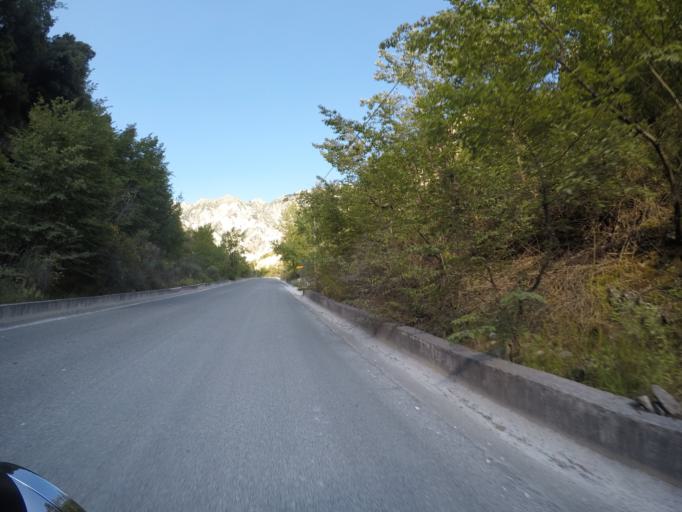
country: IT
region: Tuscany
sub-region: Provincia di Massa-Carrara
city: Carrara
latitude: 44.1000
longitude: 10.1217
